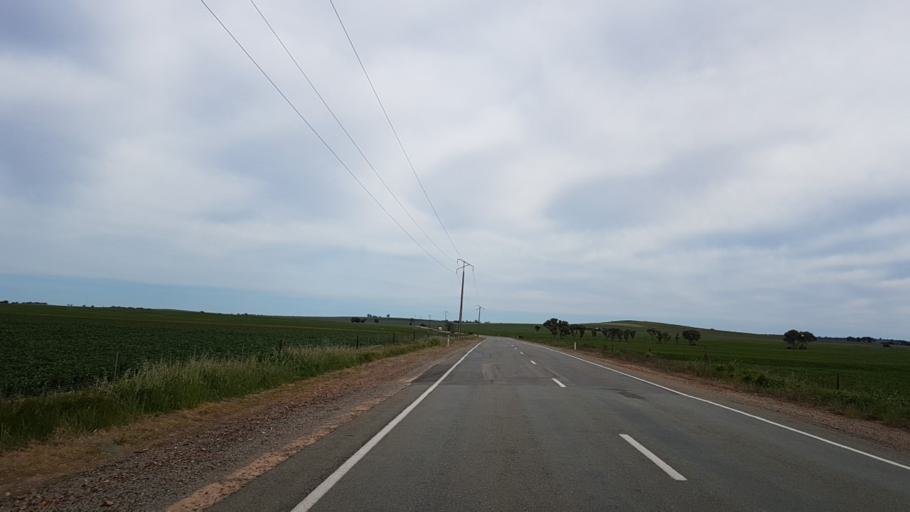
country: AU
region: South Australia
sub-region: Port Pirie City and Dists
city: Crystal Brook
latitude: -33.2659
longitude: 138.3285
